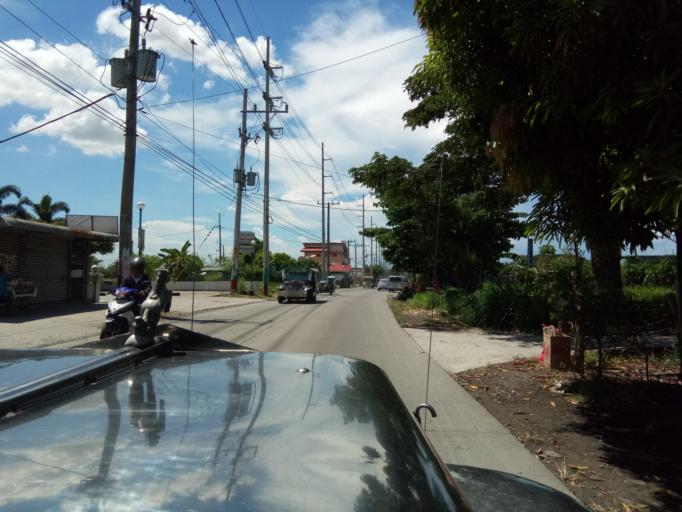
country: PH
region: Calabarzon
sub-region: Province of Cavite
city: Dasmarinas
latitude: 14.3325
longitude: 120.9100
